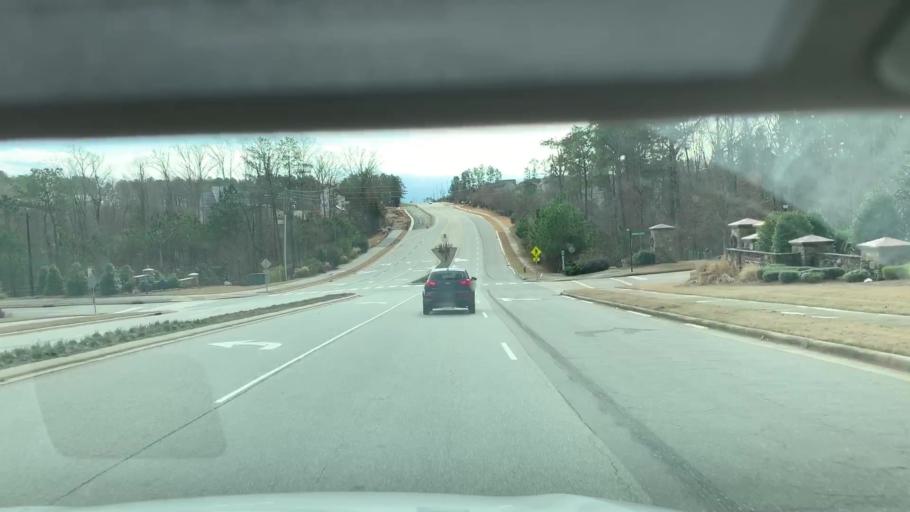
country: US
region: North Carolina
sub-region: Wake County
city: Green Level
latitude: 35.8386
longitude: -78.8998
